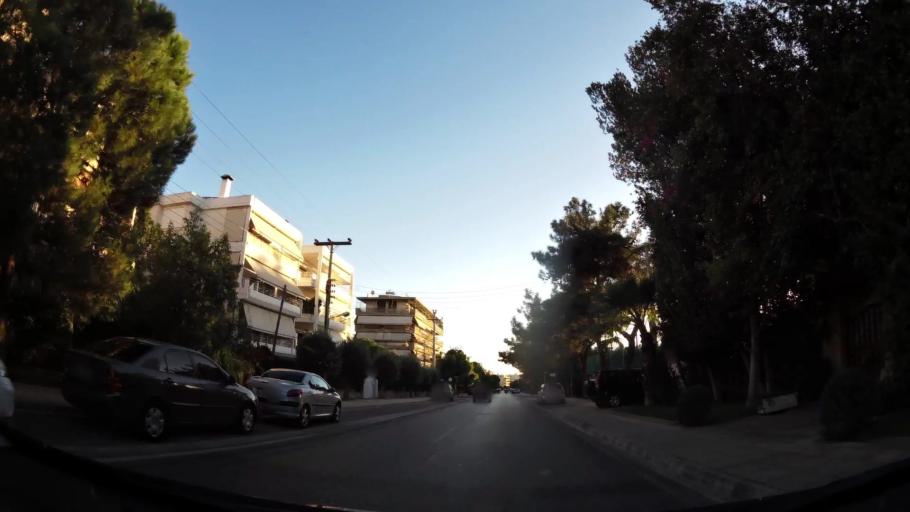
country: GR
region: Attica
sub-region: Nomarchia Athinas
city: Glyfada
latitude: 37.8748
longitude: 23.7532
